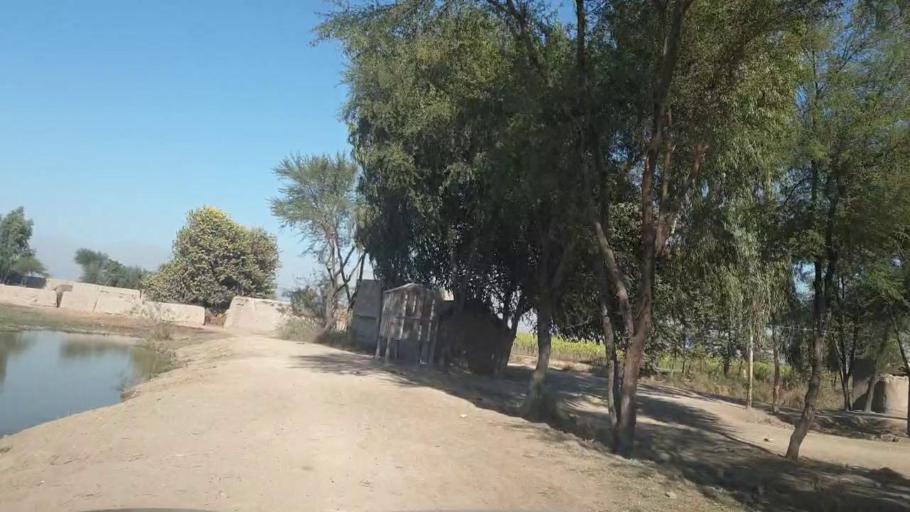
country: PK
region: Sindh
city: Mirpur Mathelo
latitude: 28.0612
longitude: 69.5101
